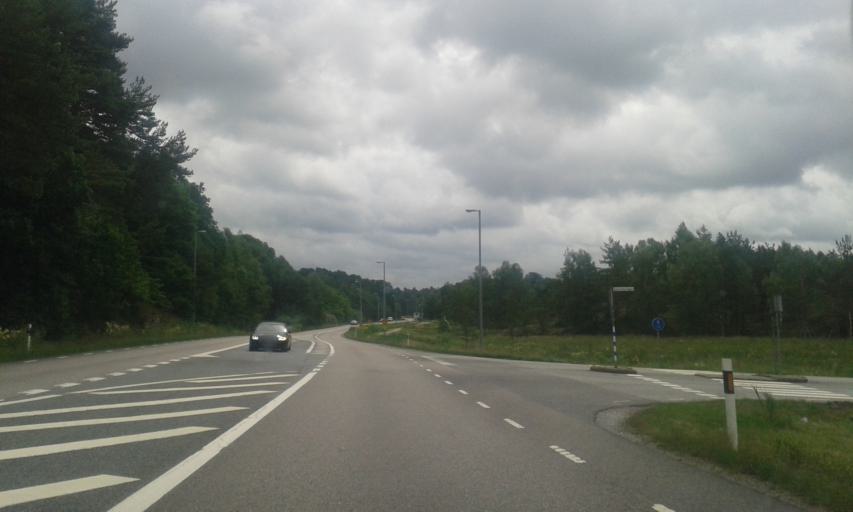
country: SE
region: Vaestra Goetaland
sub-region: Kungalvs Kommun
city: Kungalv
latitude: 57.8716
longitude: 11.9096
